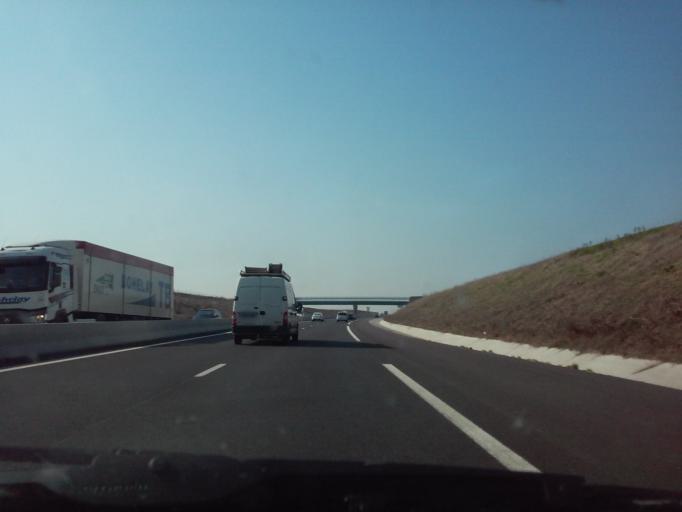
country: FR
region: Lower Normandy
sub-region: Departement du Calvados
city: Creully
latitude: 49.2271
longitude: -0.5682
